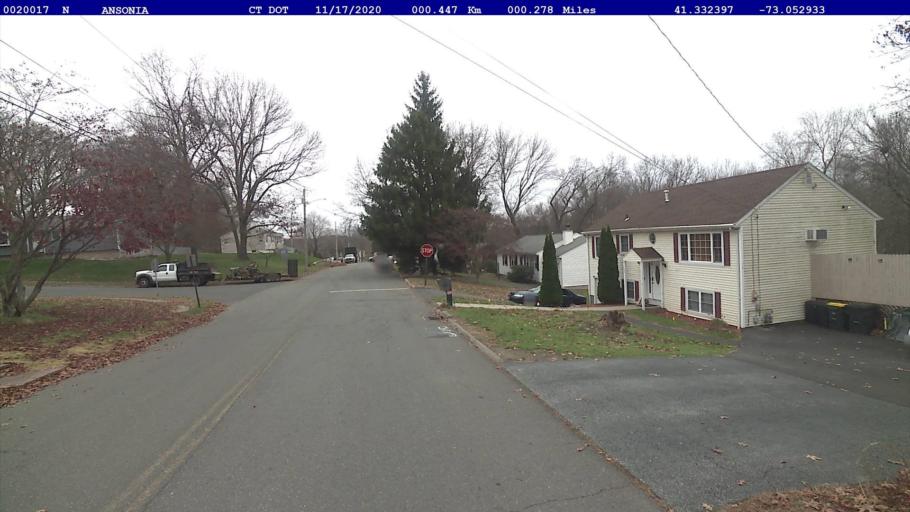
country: US
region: Connecticut
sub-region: New Haven County
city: Ansonia
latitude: 41.3324
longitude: -73.0529
